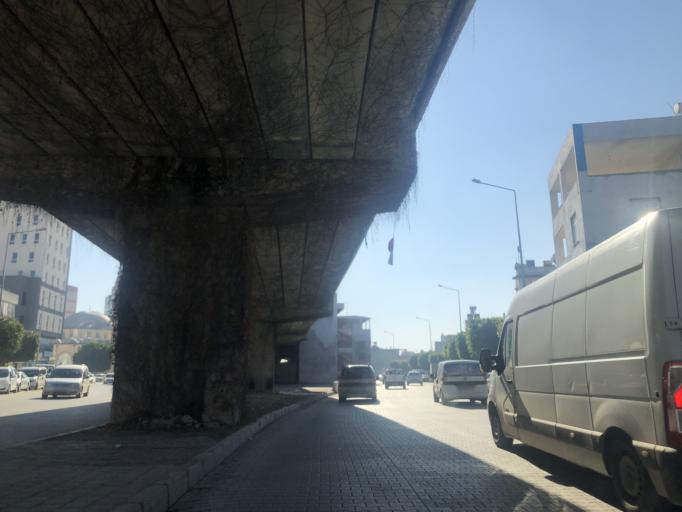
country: TR
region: Adana
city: Seyhan
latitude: 36.9858
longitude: 35.3188
